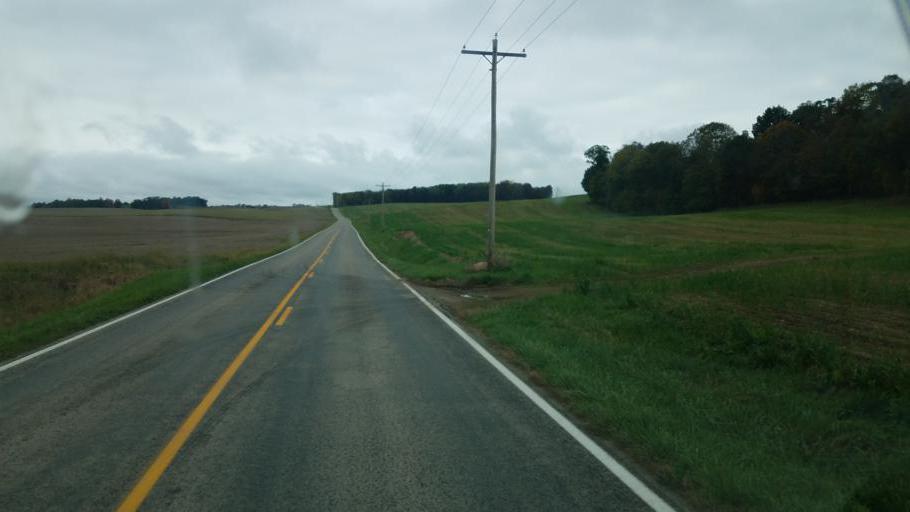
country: US
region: Ohio
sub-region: Ashland County
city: Loudonville
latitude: 40.6338
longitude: -82.2724
